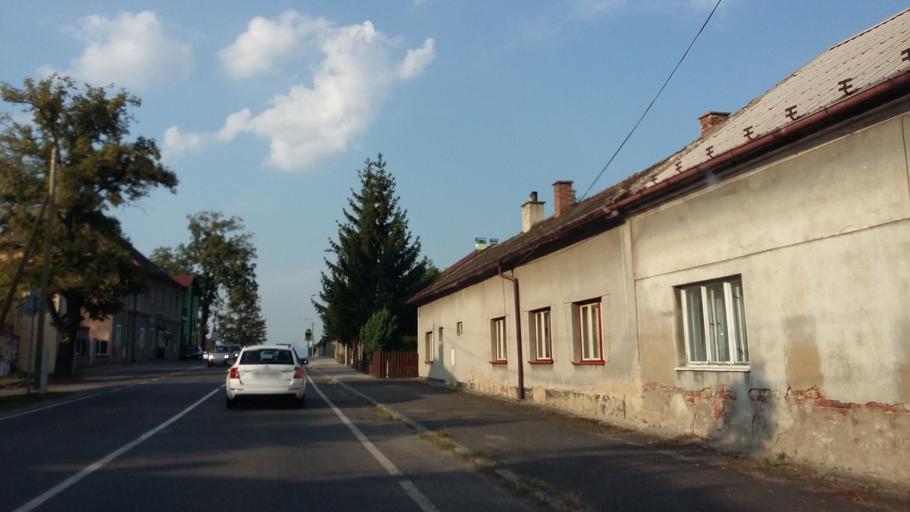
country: CZ
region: Central Bohemia
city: Kosmonosy
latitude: 50.4576
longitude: 14.9307
